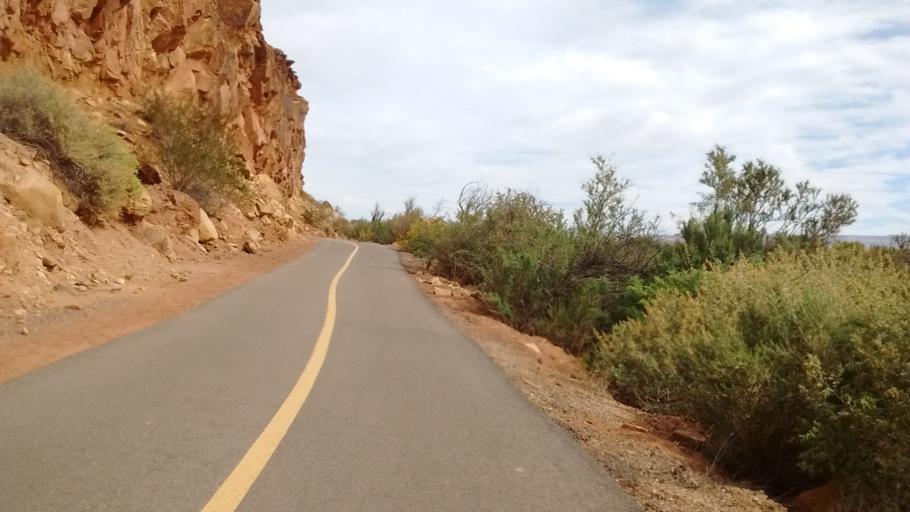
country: US
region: Utah
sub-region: Washington County
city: Washington
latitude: 37.1224
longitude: -113.4783
